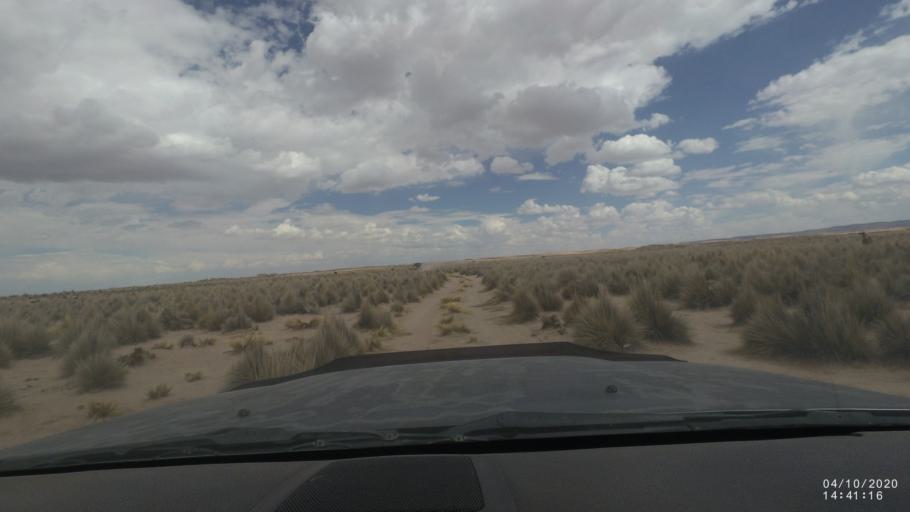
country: BO
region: Oruro
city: Poopo
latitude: -18.6819
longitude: -67.4909
